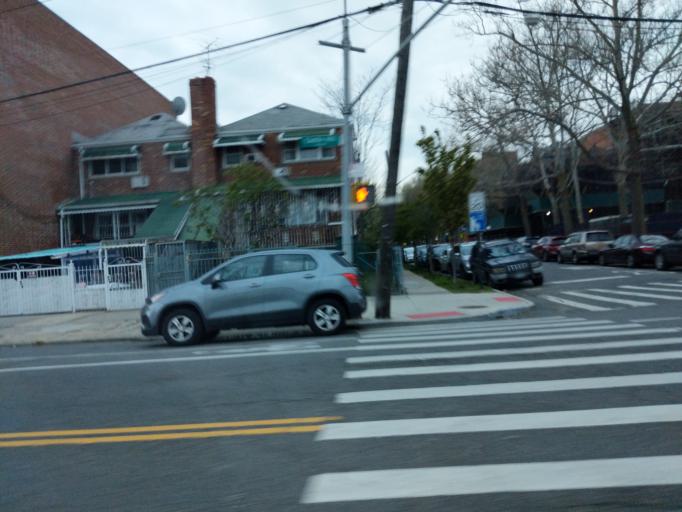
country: US
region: New York
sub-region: Bronx
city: The Bronx
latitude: 40.8377
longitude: -73.8525
